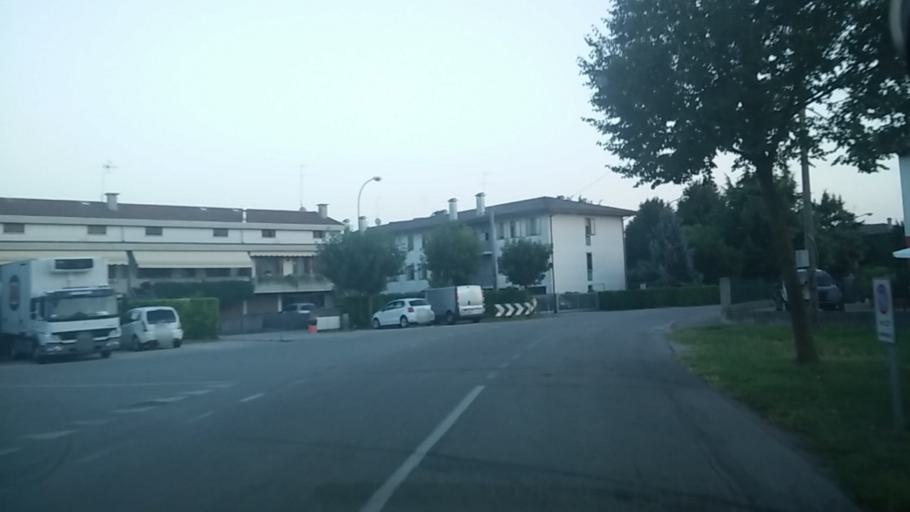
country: IT
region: Veneto
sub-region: Provincia di Venezia
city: San Dona di Piave
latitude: 45.6421
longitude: 12.5599
